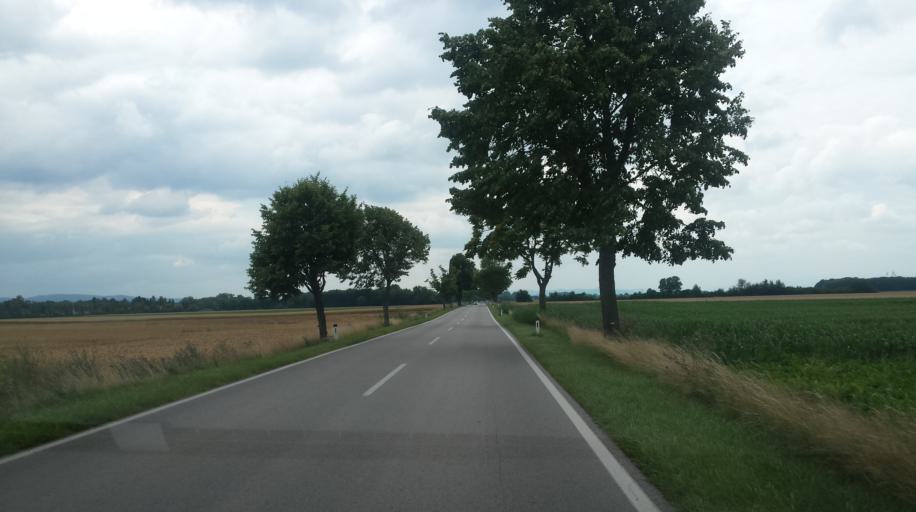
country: AT
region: Lower Austria
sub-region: Politischer Bezirk Baden
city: Mitterndorf an der Fischa
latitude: 47.9866
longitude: 16.4385
